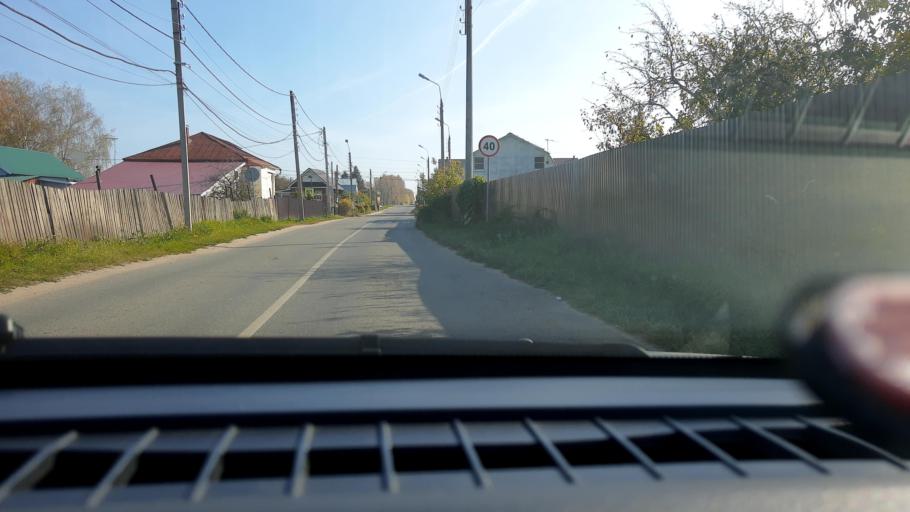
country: RU
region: Nizjnij Novgorod
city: Kstovo
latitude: 56.1575
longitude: 44.2634
